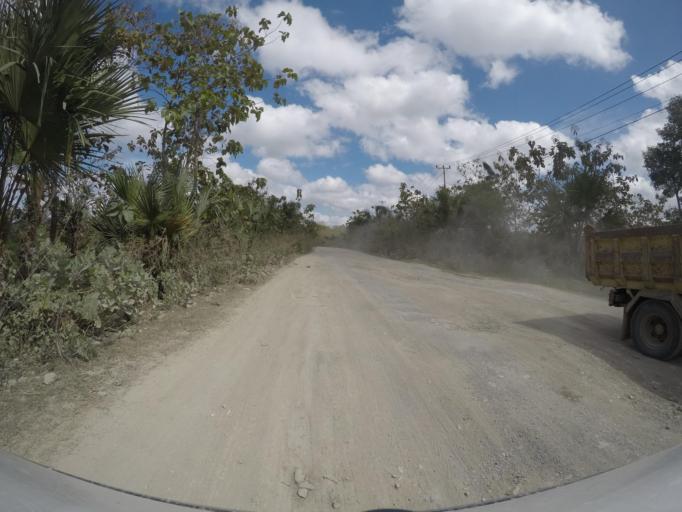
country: TL
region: Viqueque
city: Viqueque
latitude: -8.8671
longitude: 126.3407
